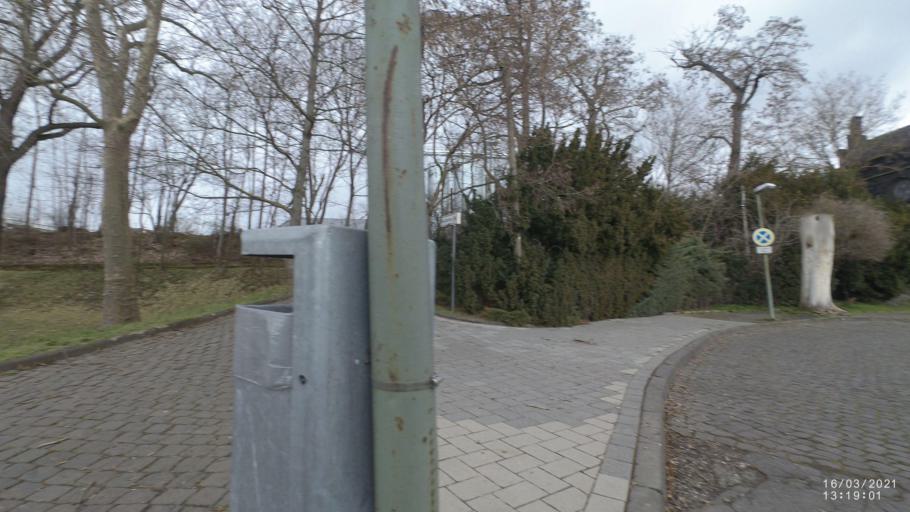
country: DE
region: Rheinland-Pfalz
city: Mendig
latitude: 50.3694
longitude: 7.2896
